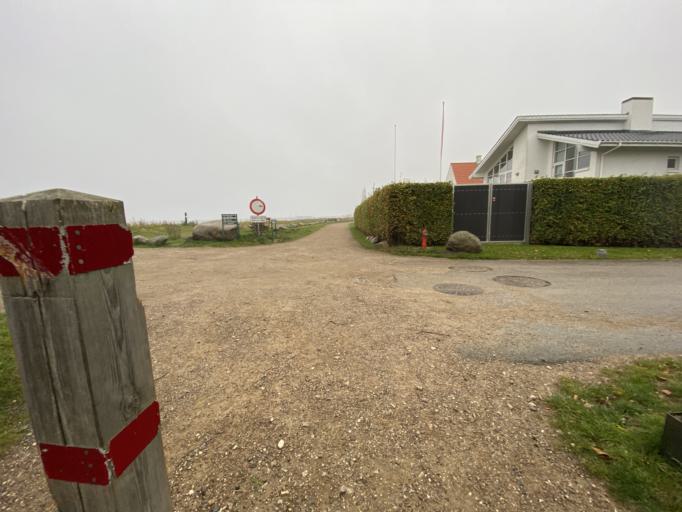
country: DK
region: Capital Region
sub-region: Dragor Kommune
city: Dragor
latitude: 55.6013
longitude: 12.6714
